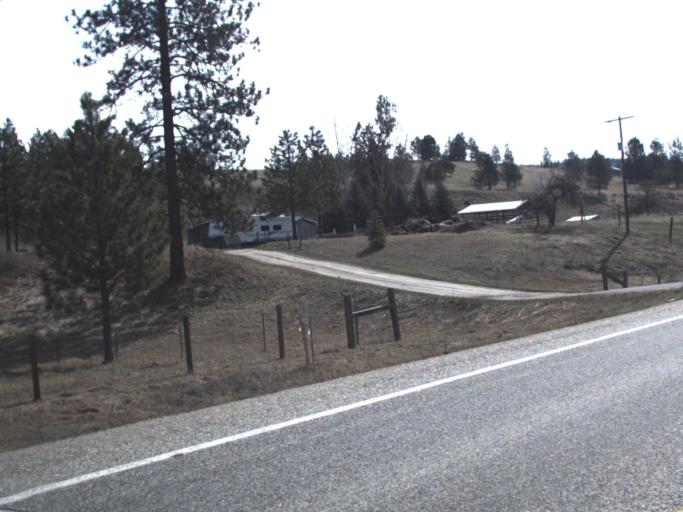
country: US
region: Washington
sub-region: Stevens County
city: Colville
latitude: 48.5226
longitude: -117.8144
